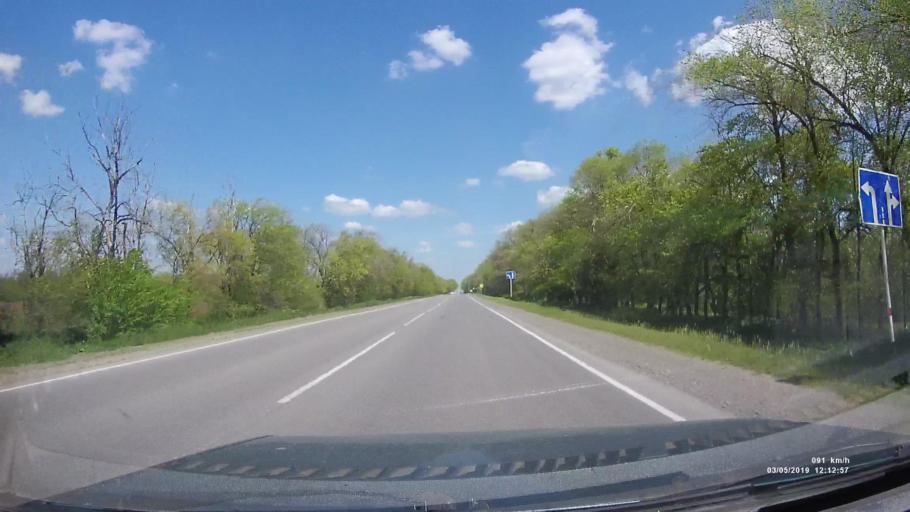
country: RU
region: Rostov
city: Bagayevskaya
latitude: 47.3274
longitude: 40.5510
